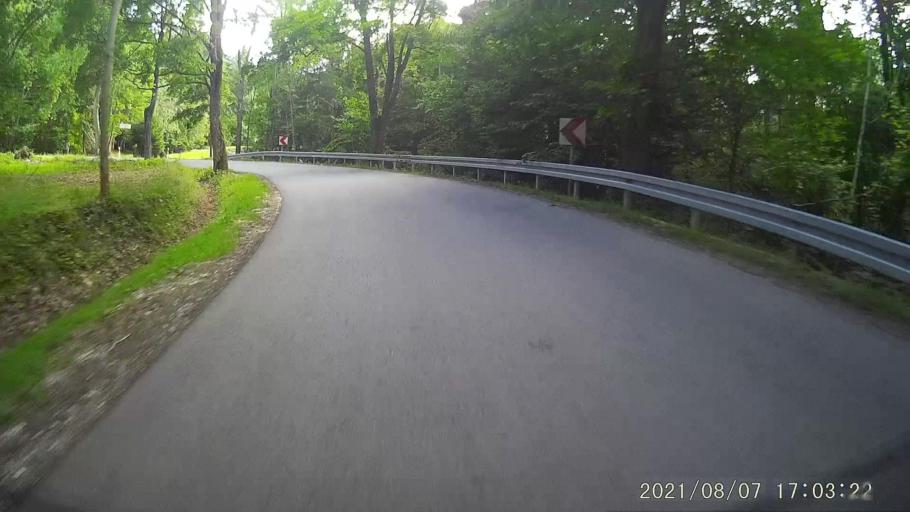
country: PL
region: Lower Silesian Voivodeship
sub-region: Powiat klodzki
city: Bystrzyca Klodzka
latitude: 50.2893
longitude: 16.5614
